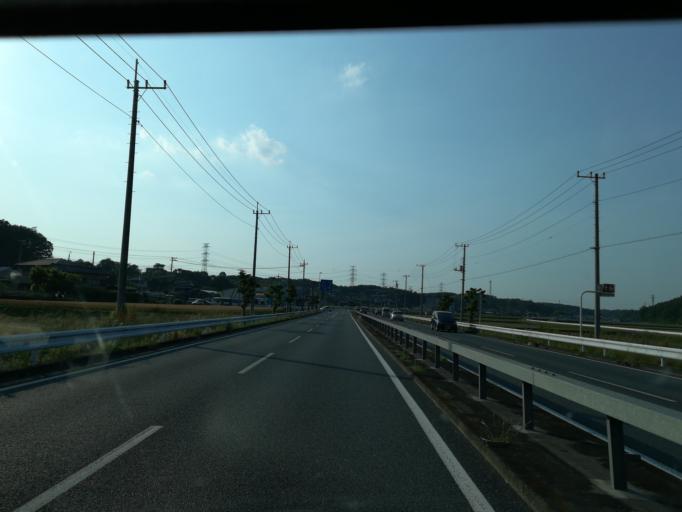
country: JP
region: Saitama
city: Kumagaya
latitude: 36.0702
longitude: 139.3607
